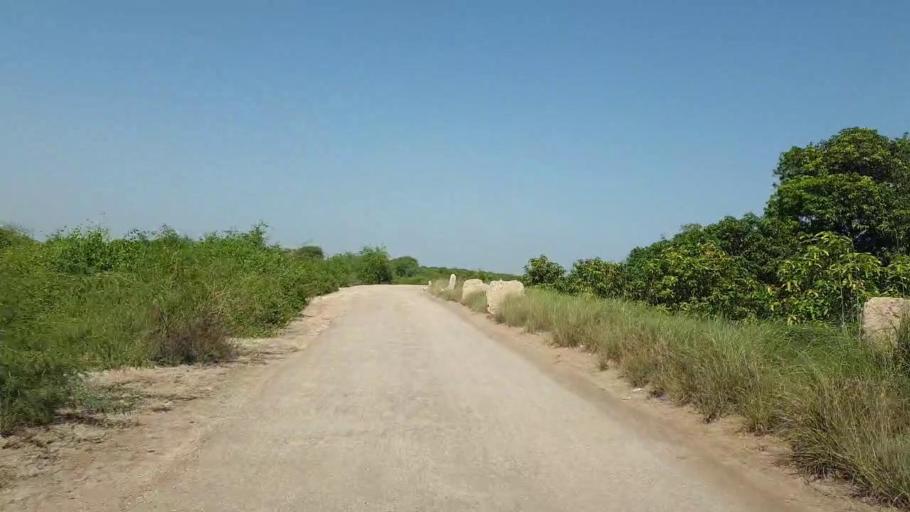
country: PK
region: Sindh
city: Tando Jam
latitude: 25.4152
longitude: 68.4562
